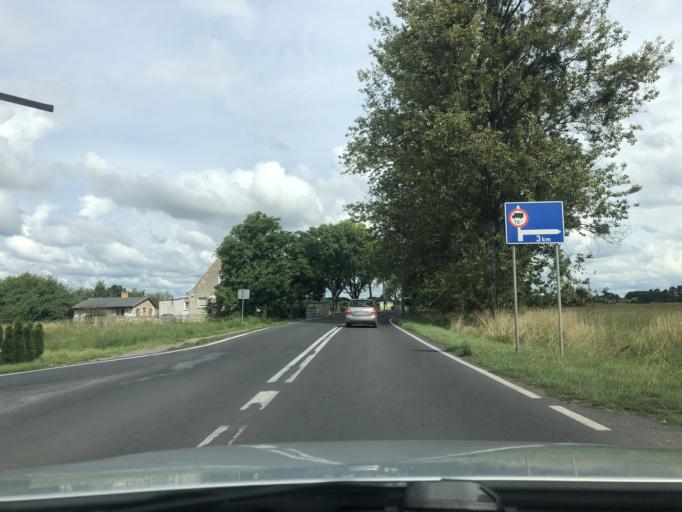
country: PL
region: Greater Poland Voivodeship
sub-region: Powiat czarnkowsko-trzcianecki
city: Krzyz Wielkopolski
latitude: 52.8847
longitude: 16.0181
